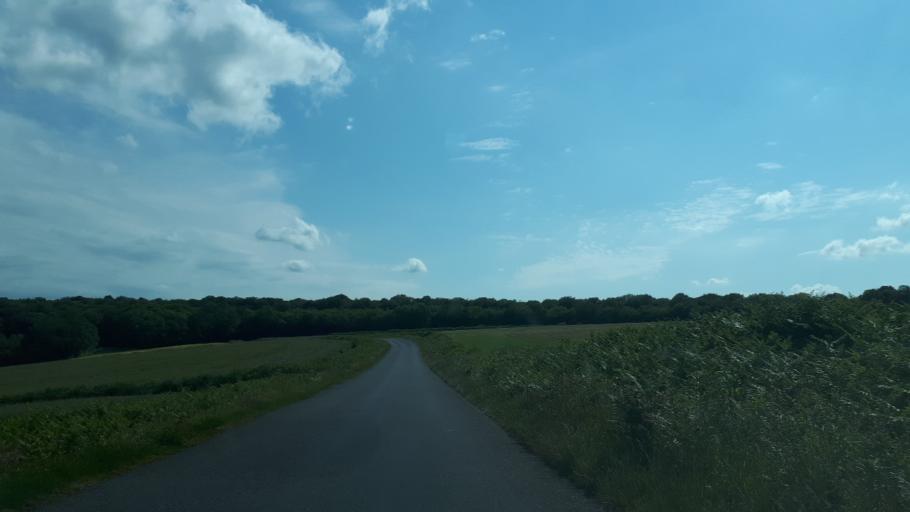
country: FR
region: Centre
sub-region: Departement du Cher
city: Henrichemont
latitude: 47.4007
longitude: 2.5960
